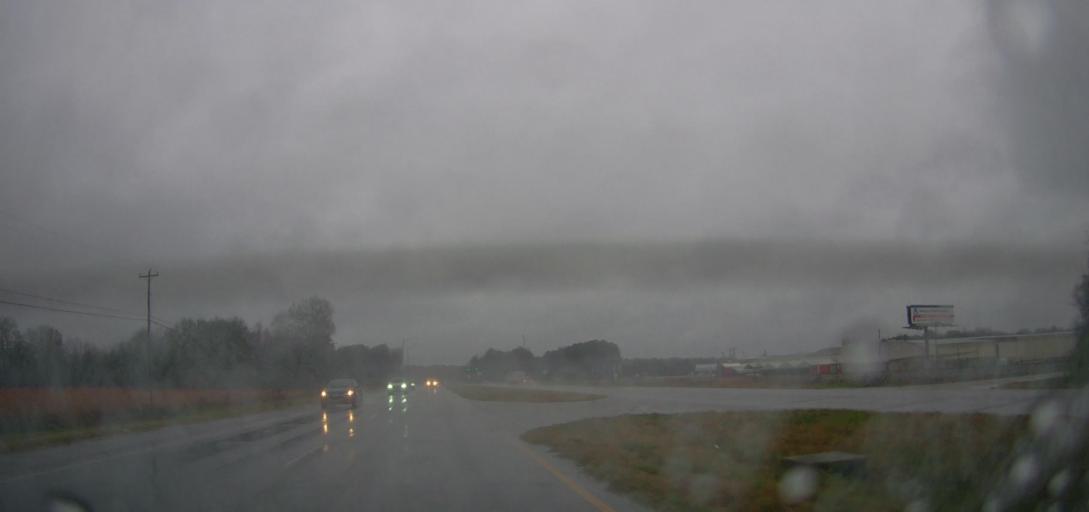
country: US
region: Alabama
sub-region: Montgomery County
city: Montgomery
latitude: 32.3736
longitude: -86.3759
